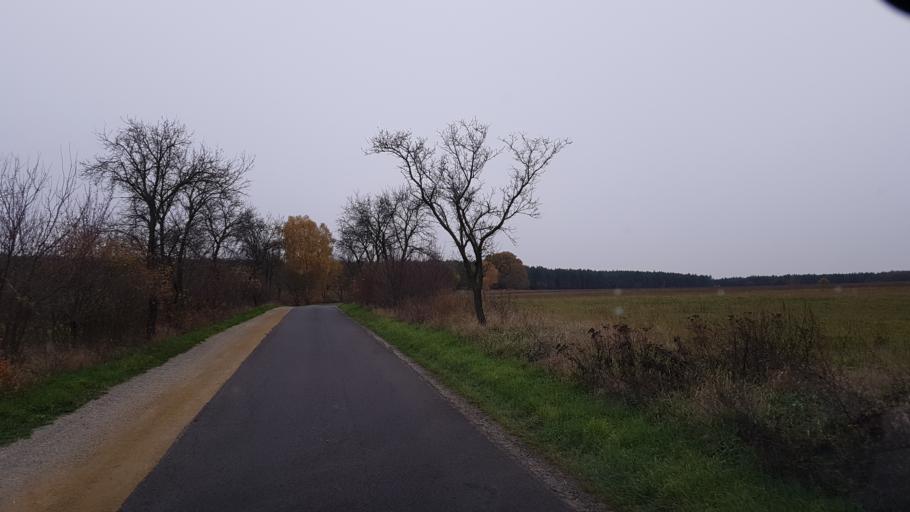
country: DE
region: Brandenburg
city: Crinitz
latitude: 51.7330
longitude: 13.7627
